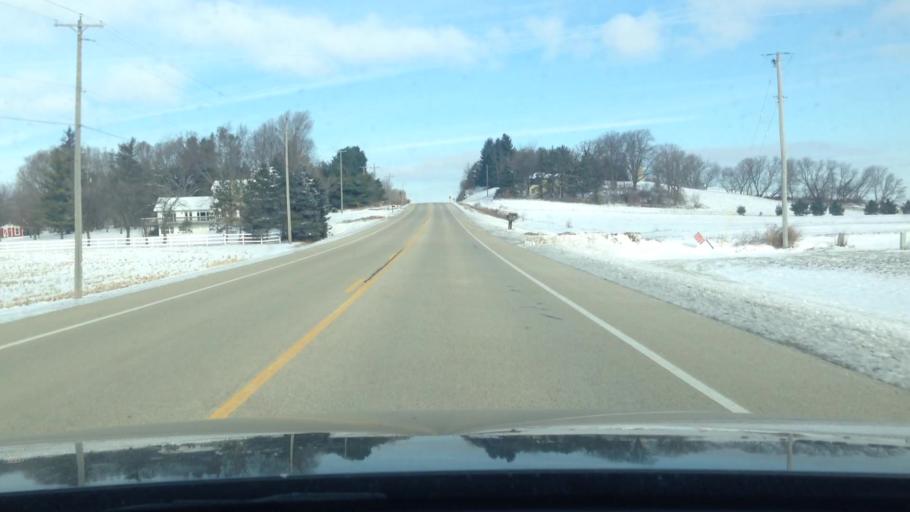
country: US
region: Wisconsin
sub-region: Walworth County
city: East Troy
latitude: 42.7545
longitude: -88.4064
